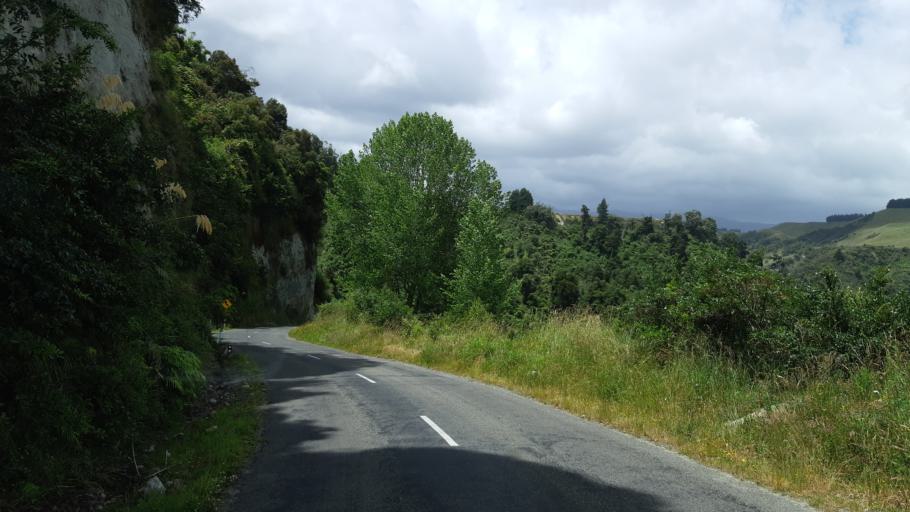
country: NZ
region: Manawatu-Wanganui
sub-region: Palmerston North City
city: Palmerston North
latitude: -39.9354
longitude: 175.9224
